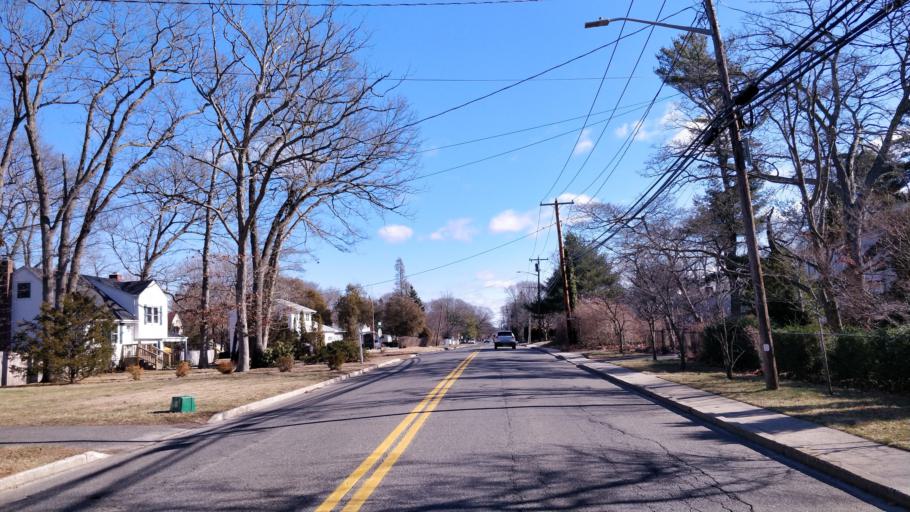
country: US
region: New York
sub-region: Suffolk County
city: Saint James
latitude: 40.8762
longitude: -73.1504
